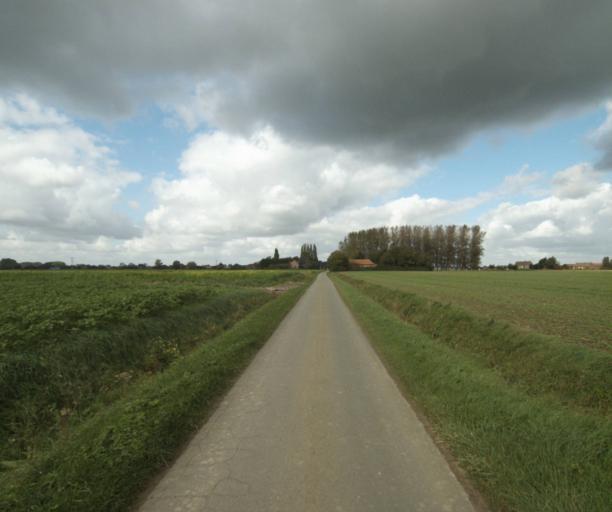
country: FR
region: Nord-Pas-de-Calais
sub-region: Departement du Nord
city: Frelinghien
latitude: 50.7047
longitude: 2.9491
